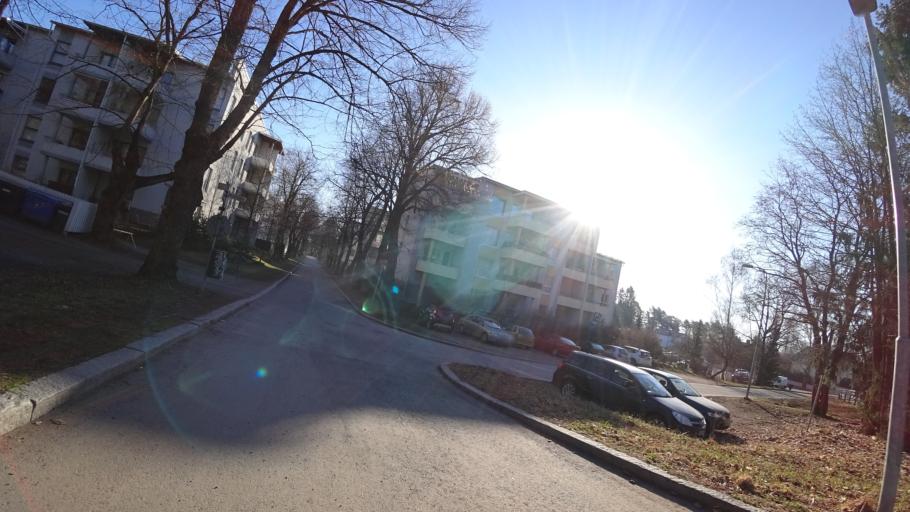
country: FI
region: Pirkanmaa
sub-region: Tampere
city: Pirkkala
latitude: 61.5047
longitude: 23.6569
